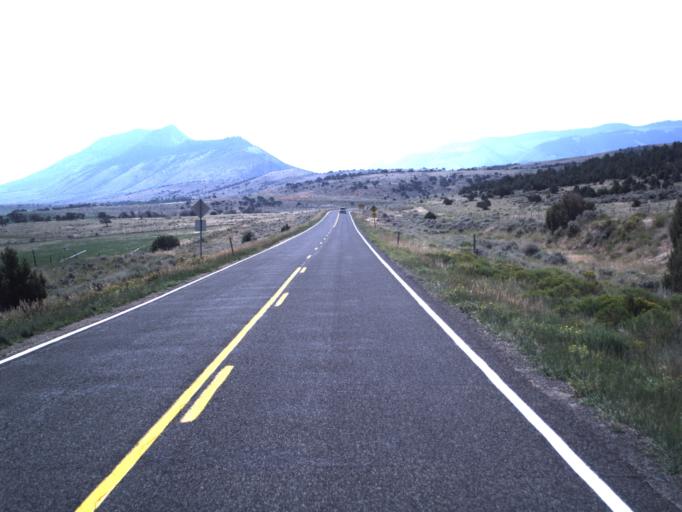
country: US
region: Utah
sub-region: Daggett County
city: Manila
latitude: 40.9892
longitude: -109.8446
